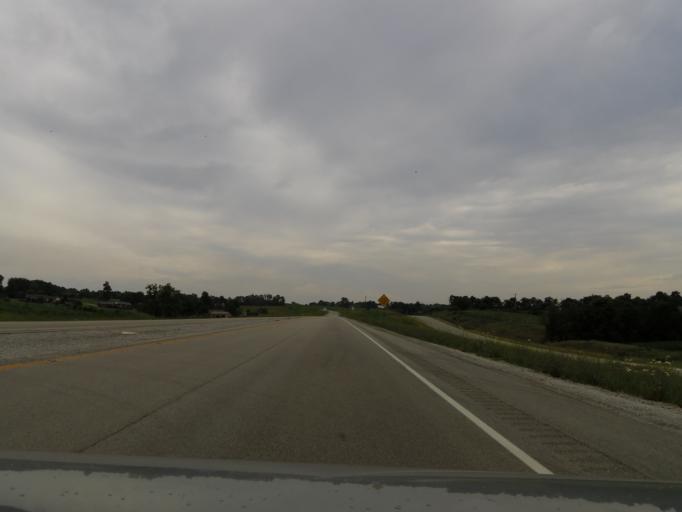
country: US
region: Ohio
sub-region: Brown County
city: Aberdeen
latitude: 38.6297
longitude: -83.8359
